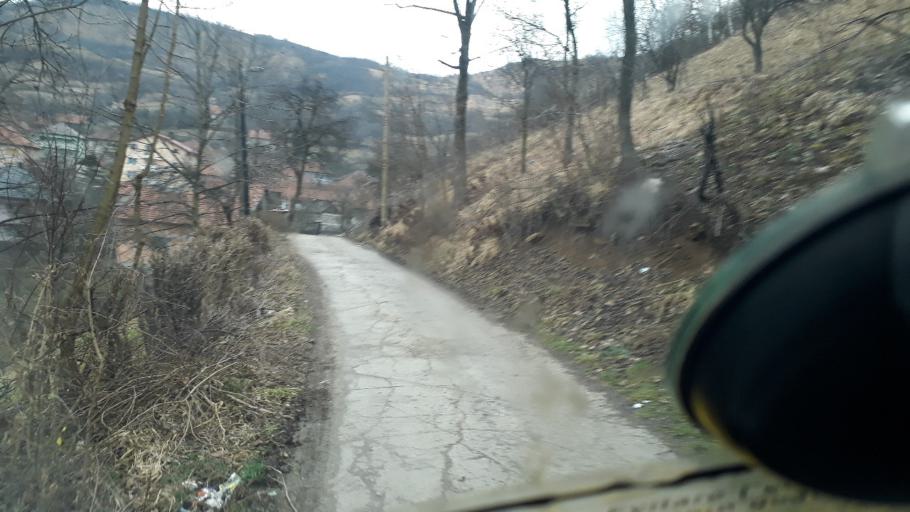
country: BA
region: Federation of Bosnia and Herzegovina
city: Zenica
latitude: 44.1506
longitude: 17.9695
